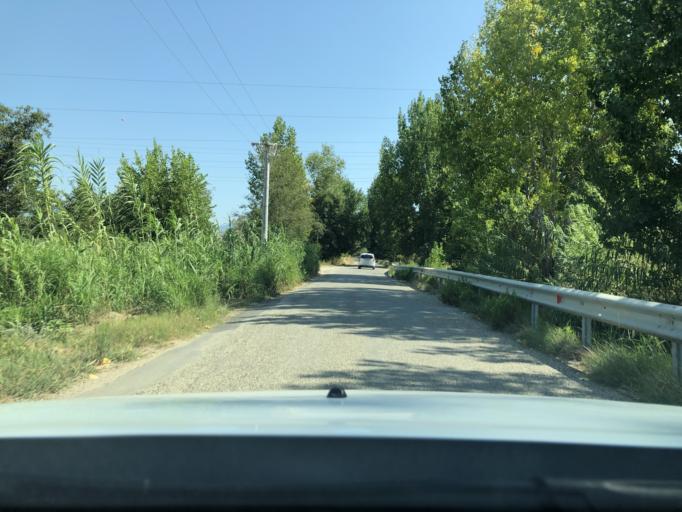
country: TR
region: Antalya
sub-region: Manavgat
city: Manavgat
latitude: 36.7978
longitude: 31.4656
